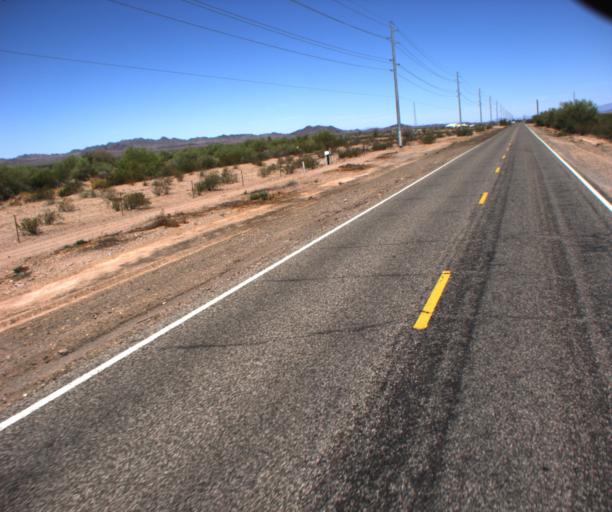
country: US
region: Arizona
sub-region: La Paz County
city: Quartzsite
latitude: 33.9025
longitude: -113.9758
